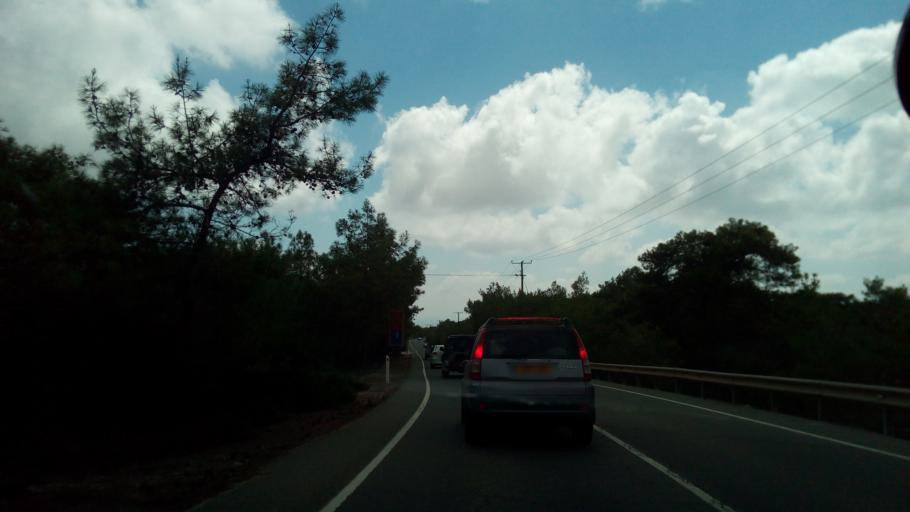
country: CY
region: Pafos
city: Pegeia
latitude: 34.8983
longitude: 32.3702
